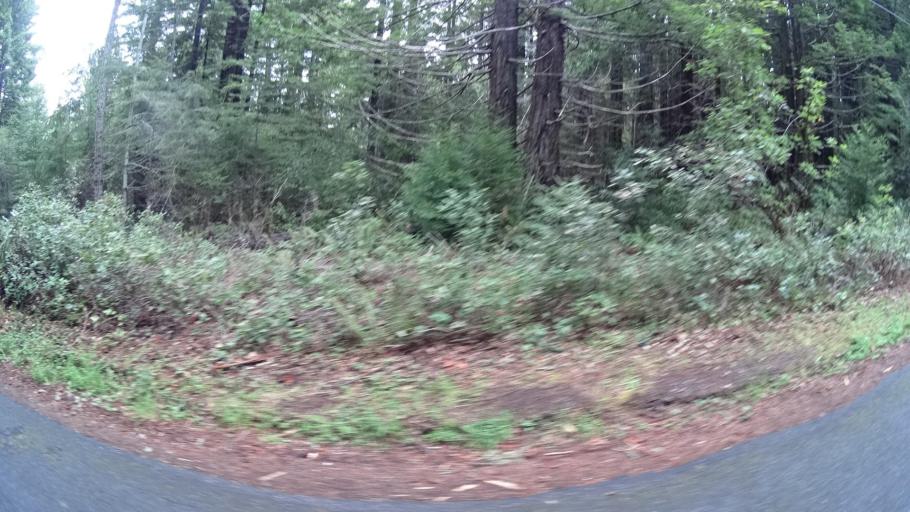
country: US
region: California
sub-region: Humboldt County
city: Blue Lake
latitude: 40.8162
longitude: -123.9941
